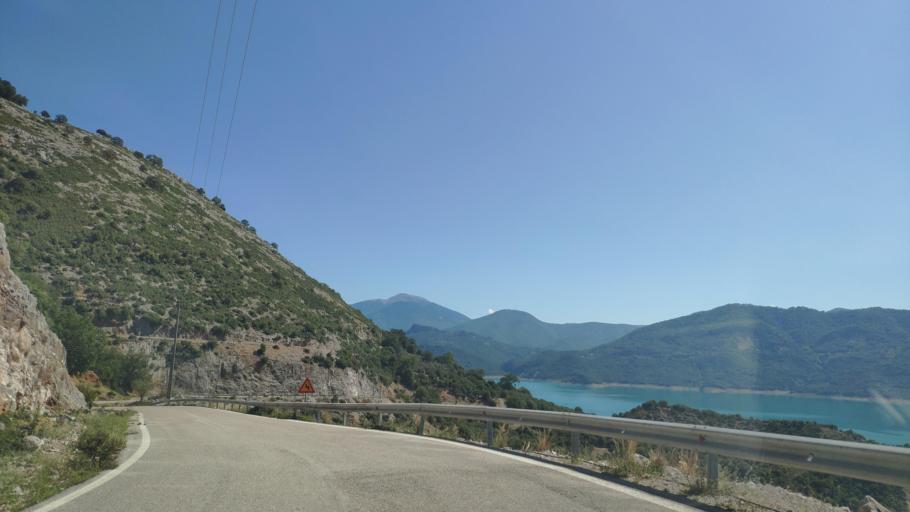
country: GR
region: Central Greece
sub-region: Nomos Evrytanias
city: Kerasochori
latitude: 38.9638
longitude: 21.4747
